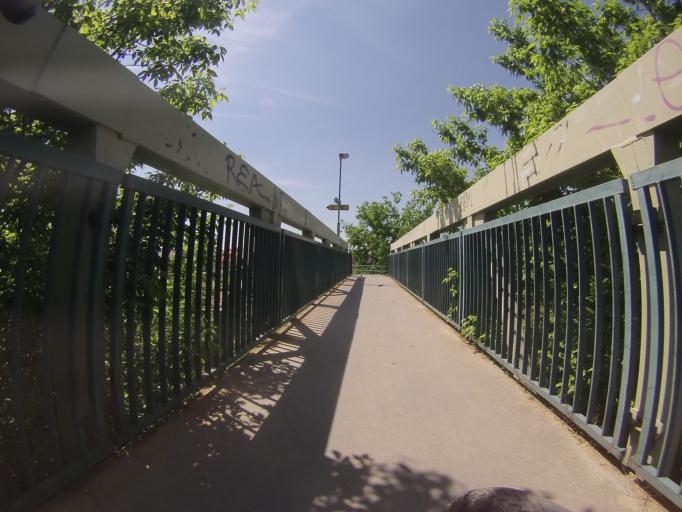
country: CZ
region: South Moravian
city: Zidlochovice
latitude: 49.0331
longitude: 16.6190
